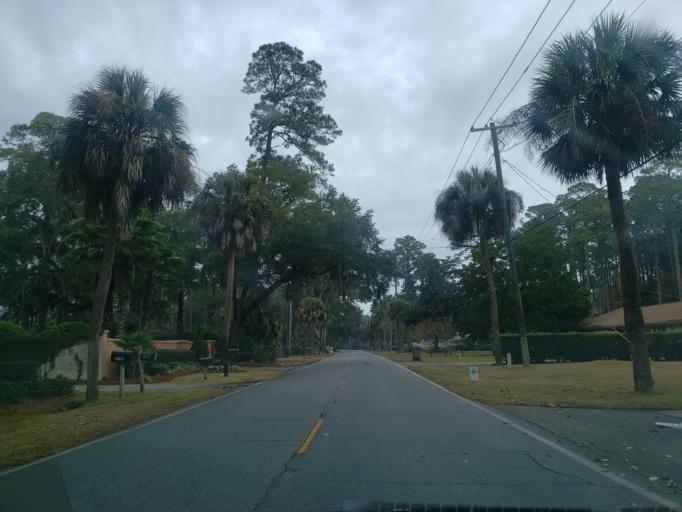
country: US
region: Georgia
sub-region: Chatham County
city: Wilmington Island
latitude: 31.9877
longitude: -80.9947
